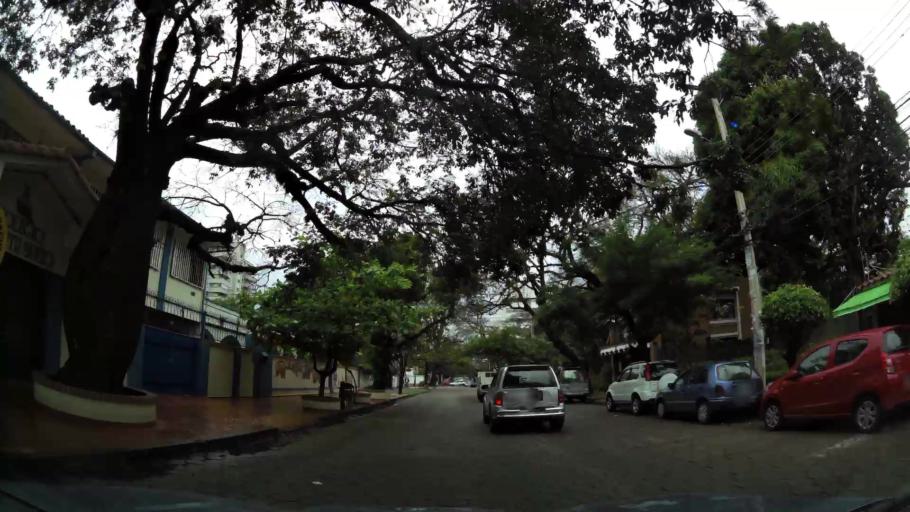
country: BO
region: Santa Cruz
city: Santa Cruz de la Sierra
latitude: -17.7937
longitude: -63.1793
